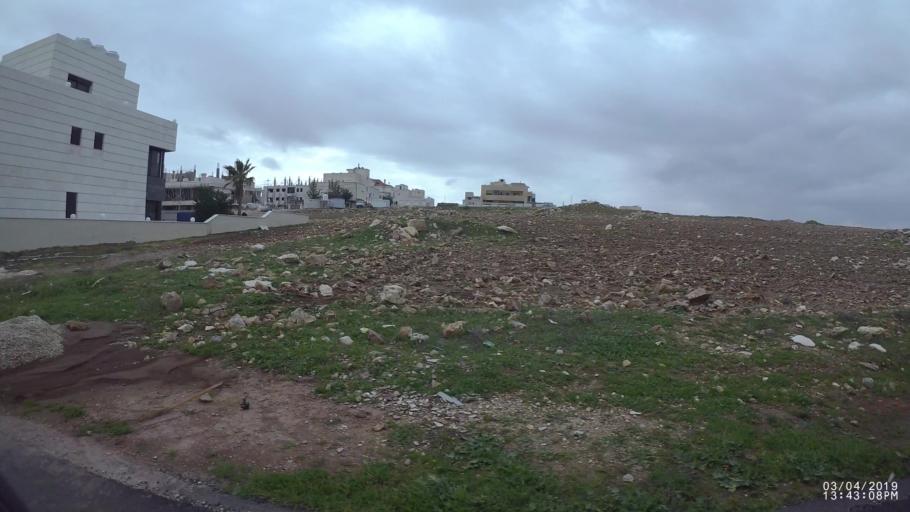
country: JO
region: Amman
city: Umm as Summaq
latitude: 31.9266
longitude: 35.8543
